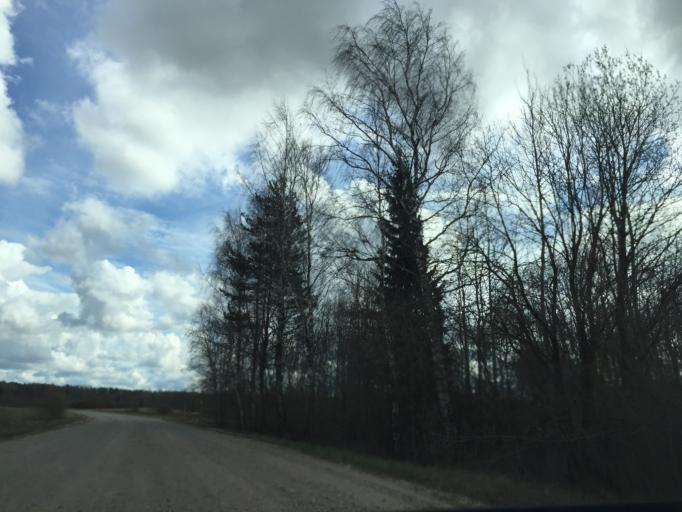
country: LV
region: Limbazu Rajons
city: Limbazi
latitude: 57.6150
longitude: 24.7786
